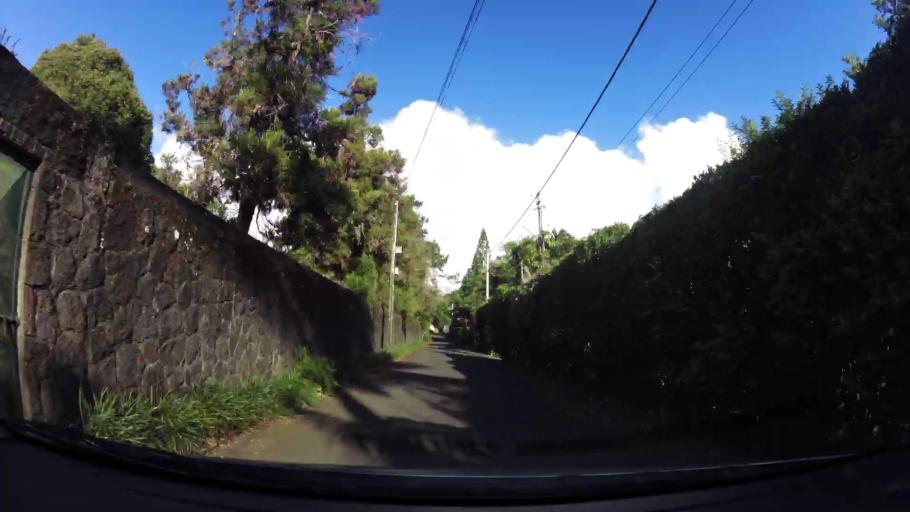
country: MU
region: Plaines Wilhems
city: Curepipe
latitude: -20.3115
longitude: 57.5020
